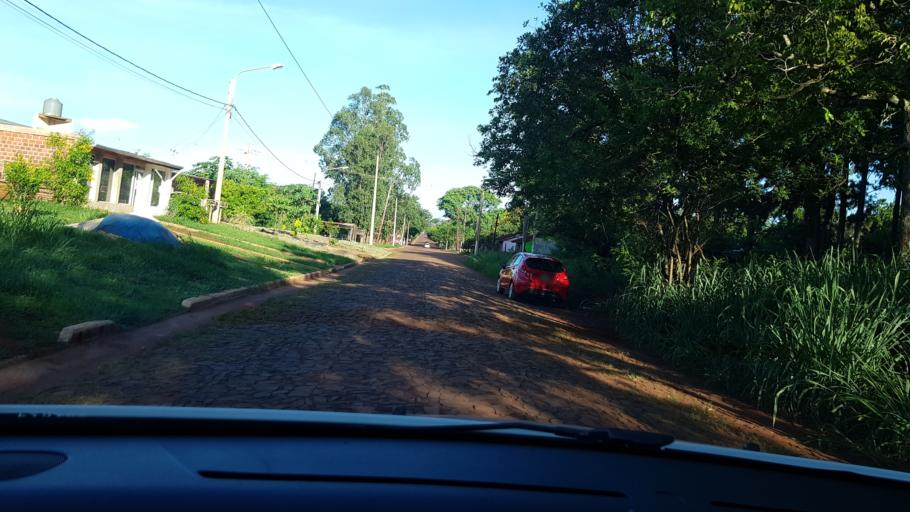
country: AR
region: Misiones
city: Puerto Libertad
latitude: -25.9206
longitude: -54.5907
